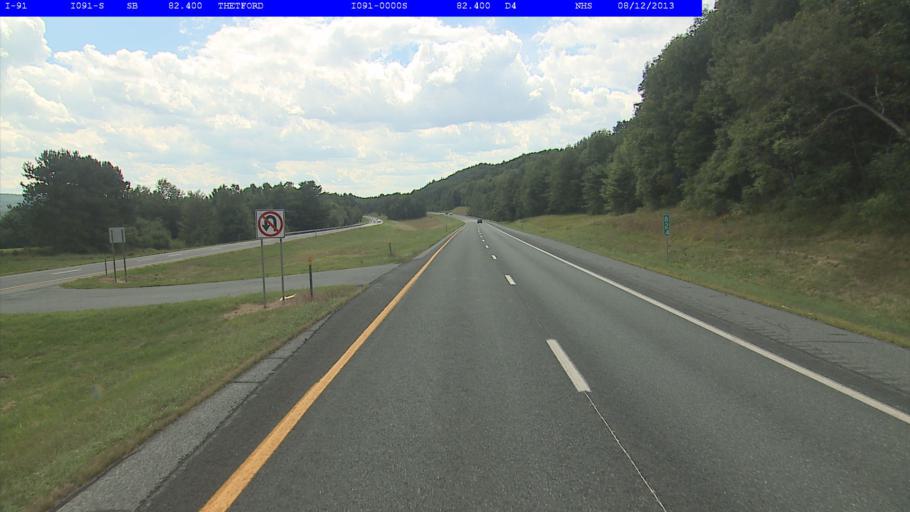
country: US
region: New Hampshire
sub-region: Grafton County
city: Lyme
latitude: 43.7879
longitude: -72.2157
